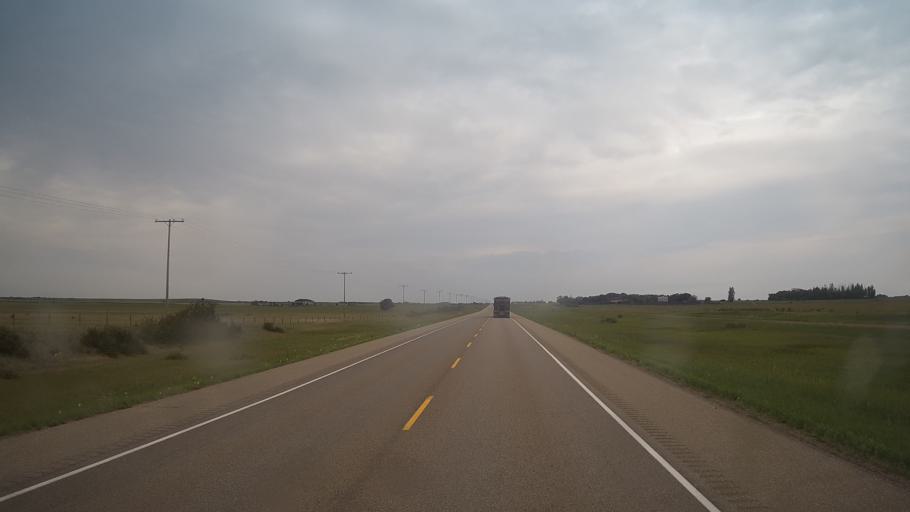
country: CA
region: Saskatchewan
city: Langham
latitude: 52.1288
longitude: -107.1577
